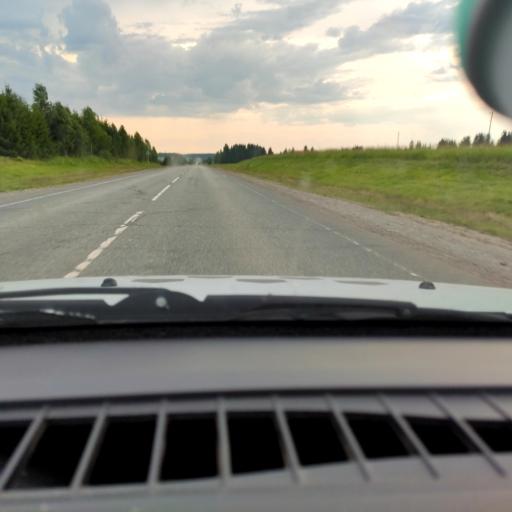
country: RU
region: Udmurtiya
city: Debesy
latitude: 57.6123
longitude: 53.5542
